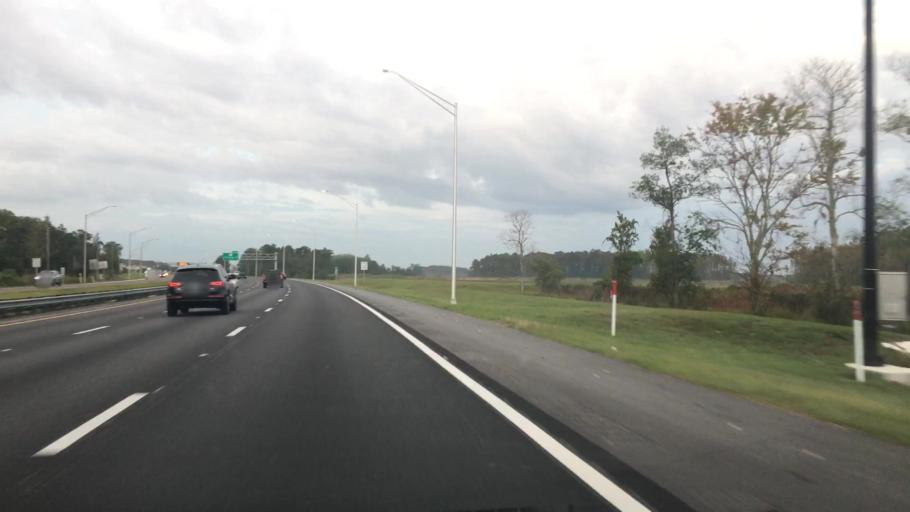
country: US
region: Florida
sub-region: Orange County
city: Conway
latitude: 28.4503
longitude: -81.2476
